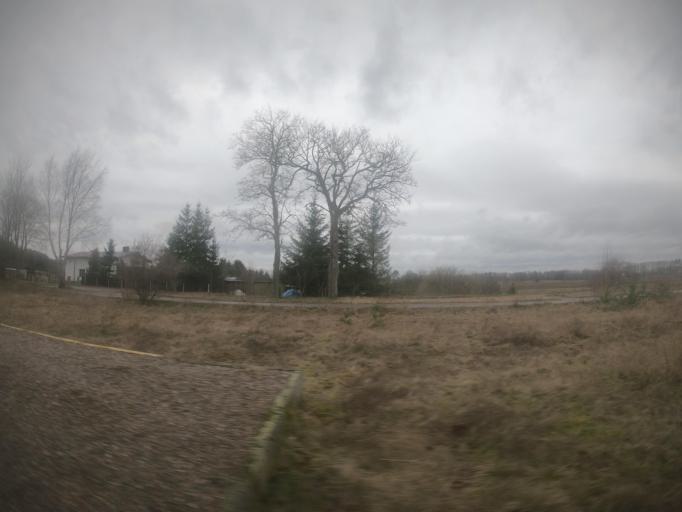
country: PL
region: West Pomeranian Voivodeship
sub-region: Powiat szczecinecki
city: Bialy Bor
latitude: 53.8078
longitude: 16.8664
